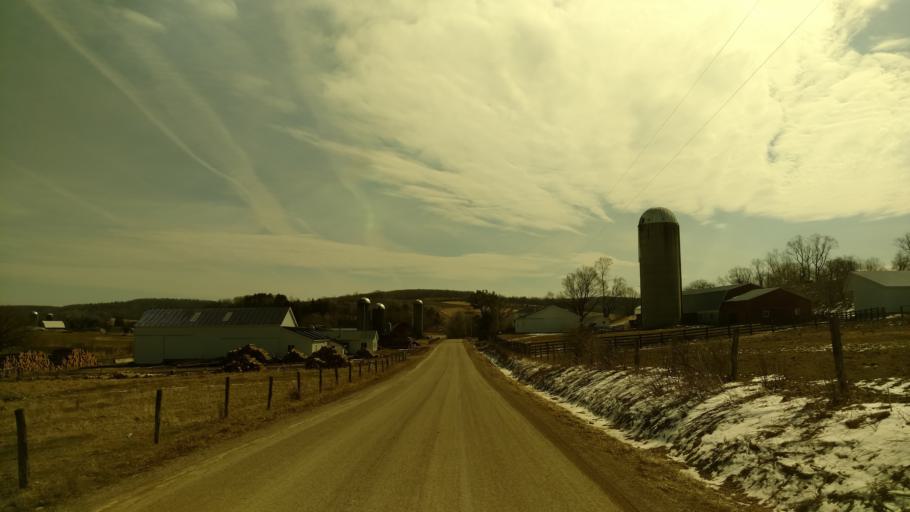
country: US
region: Pennsylvania
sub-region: Tioga County
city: Westfield
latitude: 41.9214
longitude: -77.7543
